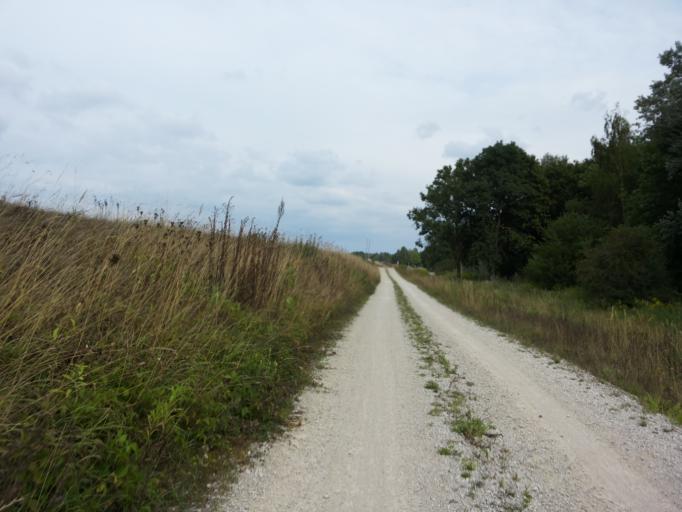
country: DE
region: Bavaria
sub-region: Upper Bavaria
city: Bergheim
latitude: 48.7504
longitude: 11.2637
